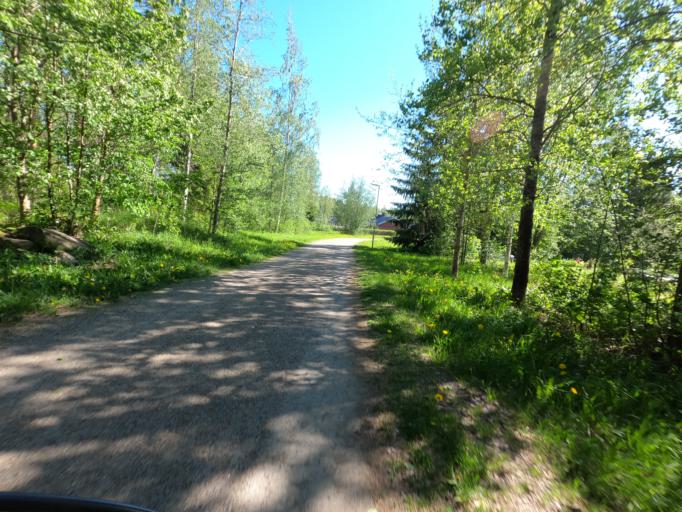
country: FI
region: North Karelia
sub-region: Joensuu
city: Joensuu
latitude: 62.5892
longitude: 29.8001
